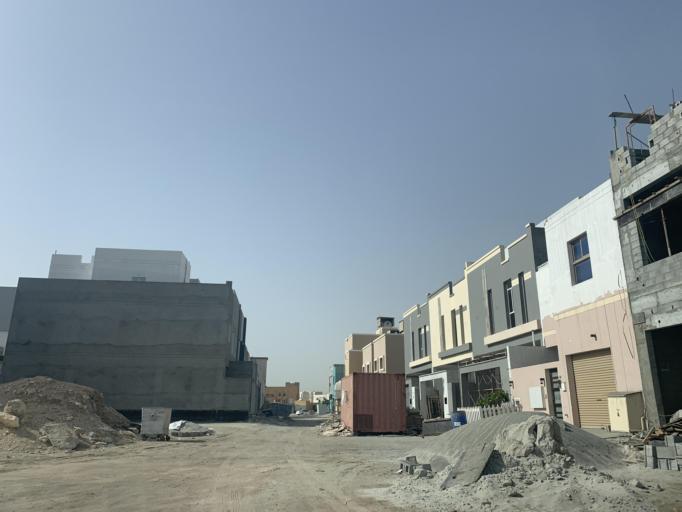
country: BH
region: Northern
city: Sitrah
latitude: 26.1630
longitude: 50.6058
